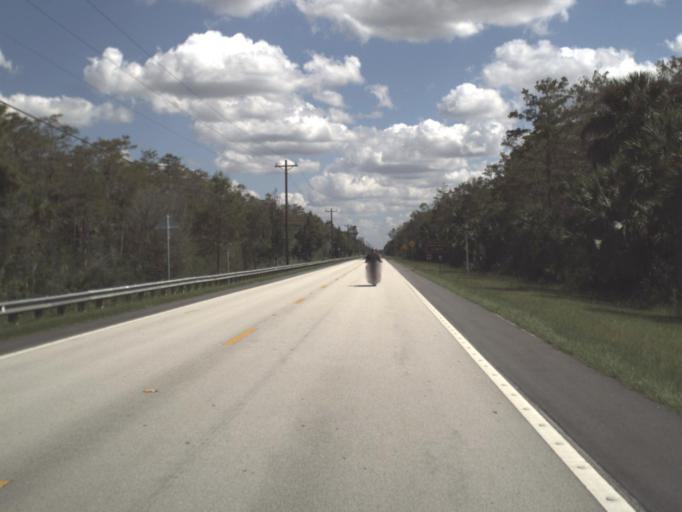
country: US
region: Florida
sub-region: Collier County
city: Marco
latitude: 25.8938
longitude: -81.2765
